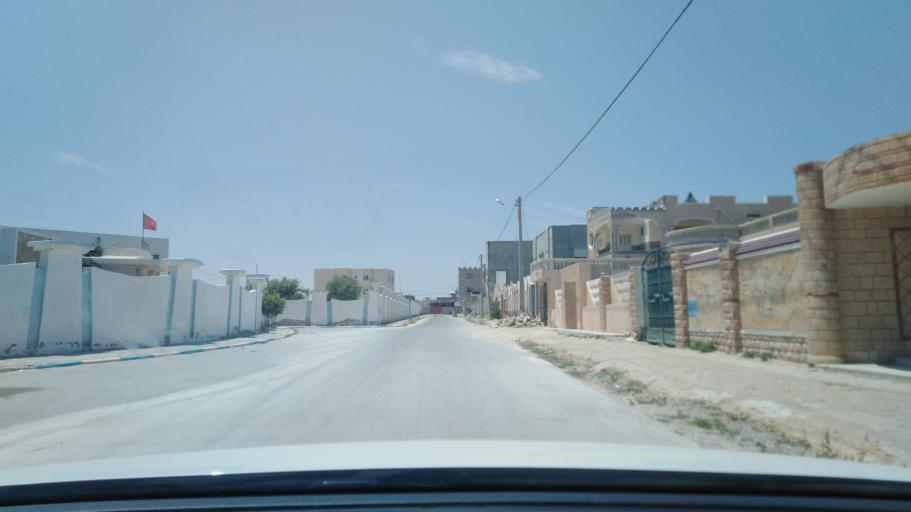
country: TN
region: Qabis
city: Gabes
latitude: 33.9507
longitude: 10.0711
